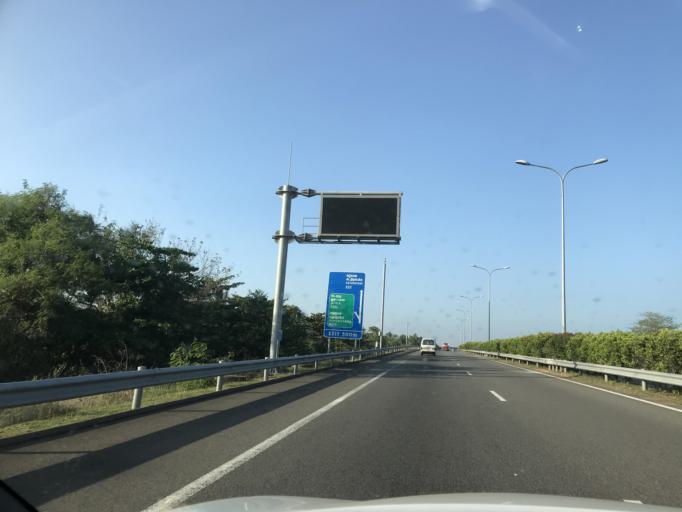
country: LK
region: Western
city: Ja Ela
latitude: 7.0745
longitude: 79.8778
